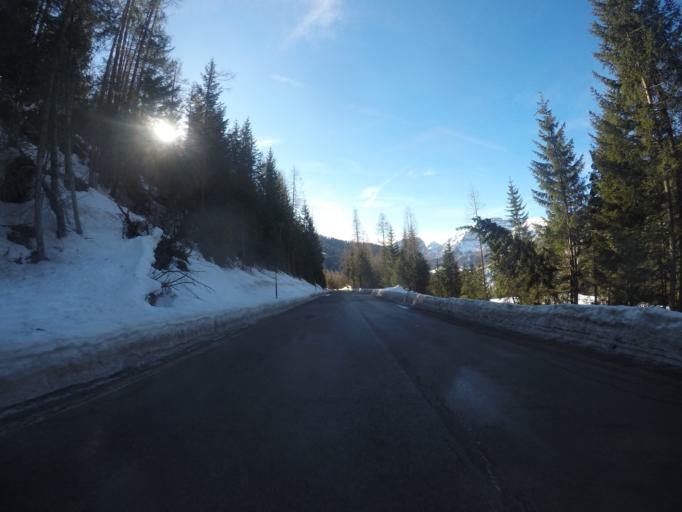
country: IT
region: Veneto
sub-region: Provincia di Belluno
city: Livinallongo del Col di Lana
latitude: 46.4932
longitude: 11.9895
